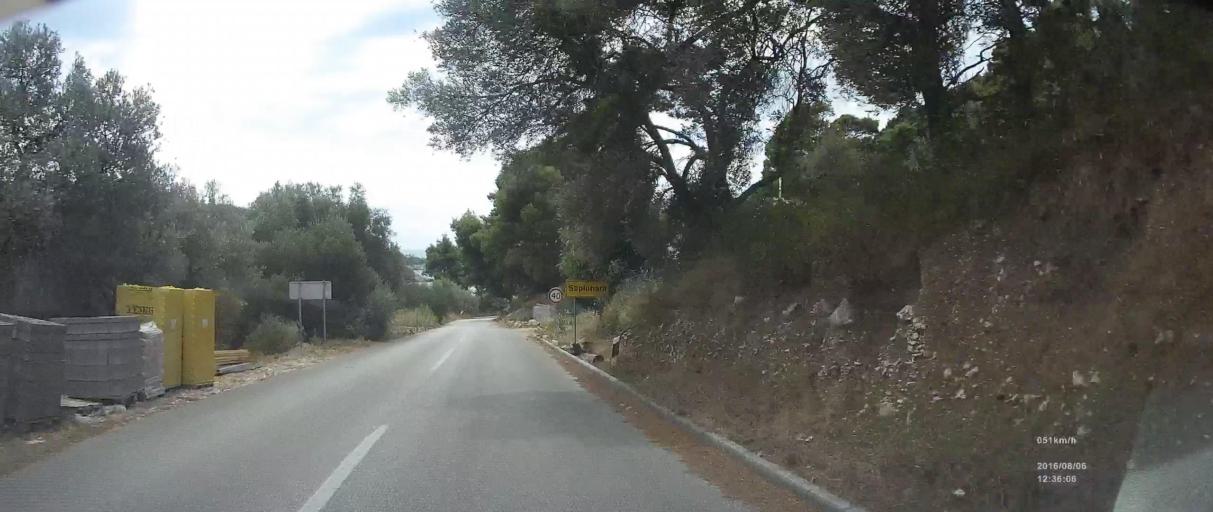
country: HR
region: Dubrovacko-Neretvanska
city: Ston
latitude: 42.7031
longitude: 17.7362
